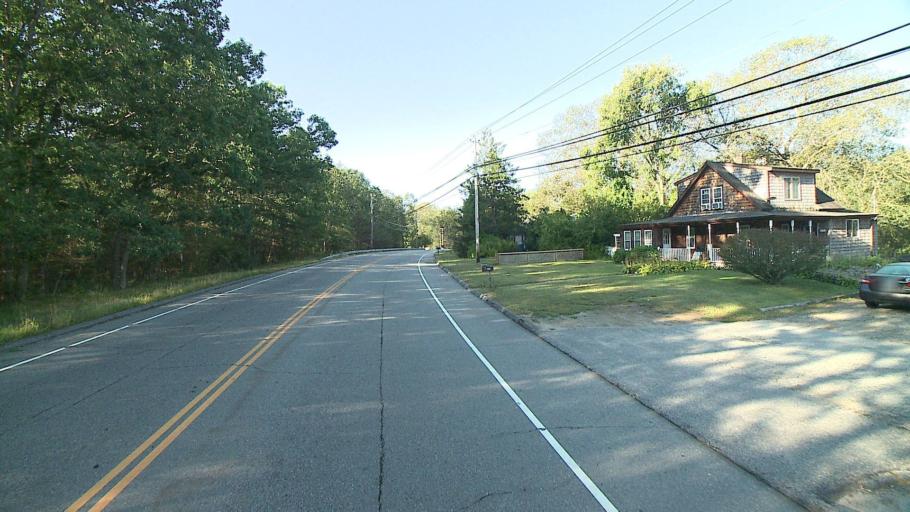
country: US
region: Connecticut
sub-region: Windham County
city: East Brooklyn
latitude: 41.7863
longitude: -71.8856
